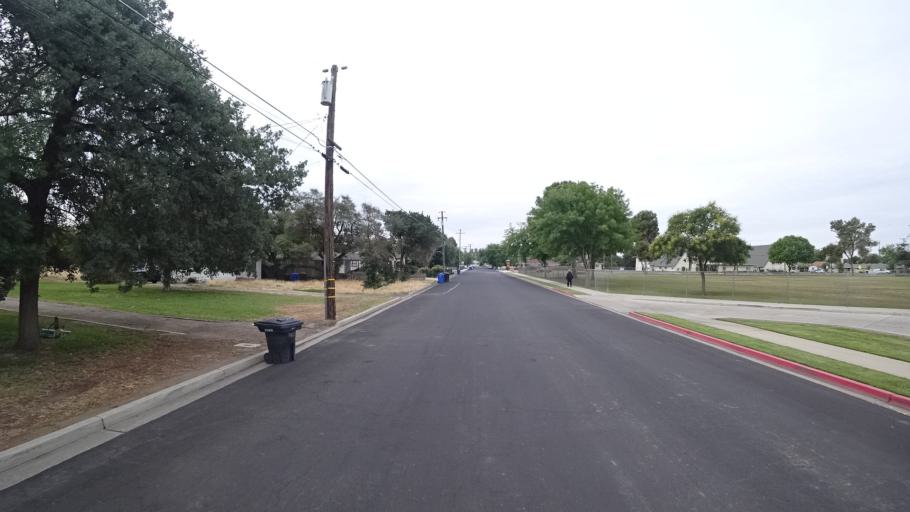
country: US
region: California
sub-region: Kings County
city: Hanford
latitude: 36.3376
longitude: -119.6521
